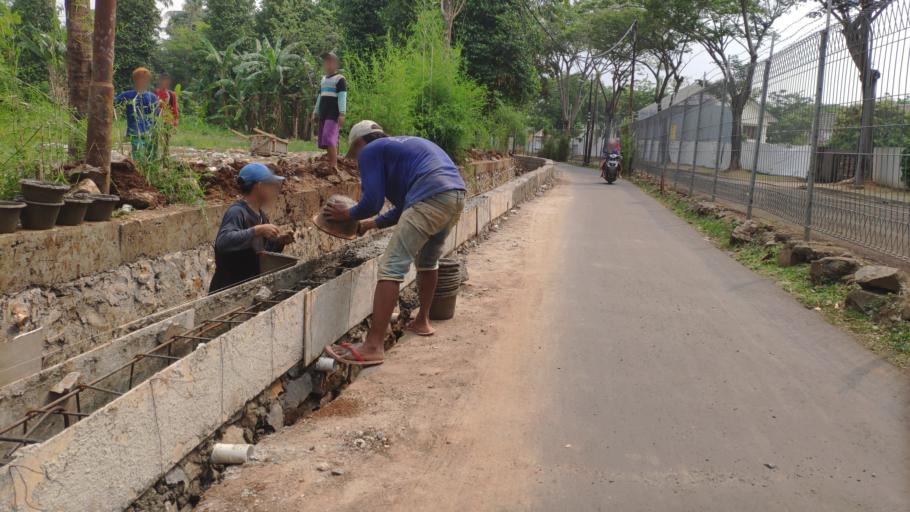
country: ID
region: West Java
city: Depok
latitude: -6.3396
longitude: 106.8172
